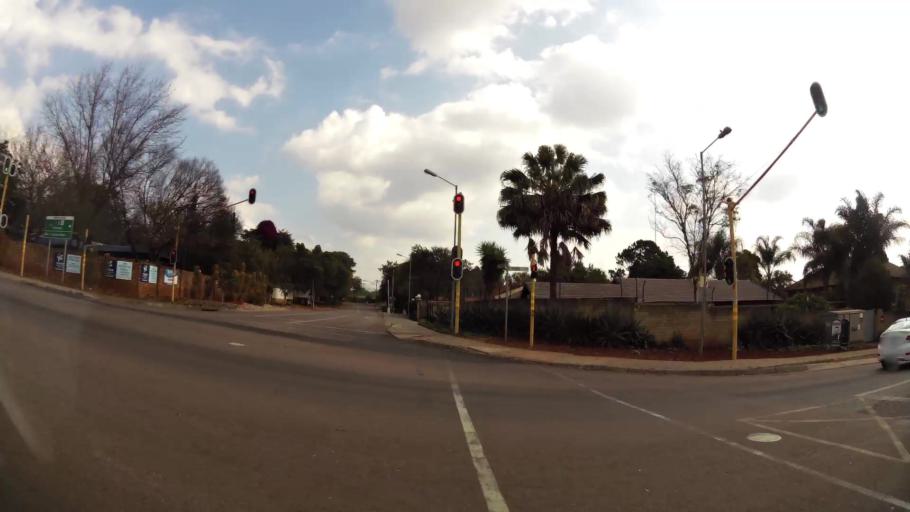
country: ZA
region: Gauteng
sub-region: City of Tshwane Metropolitan Municipality
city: Pretoria
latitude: -25.7488
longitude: 28.2890
